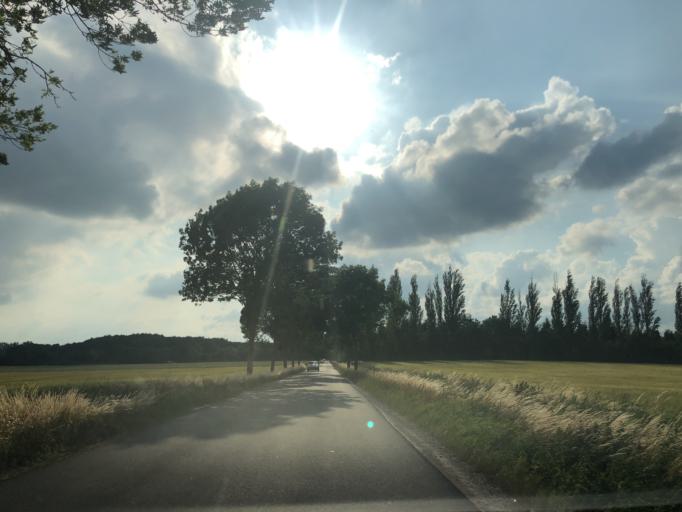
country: DK
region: Zealand
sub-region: Faxe Kommune
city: Ronnede
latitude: 55.3080
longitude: 12.0377
